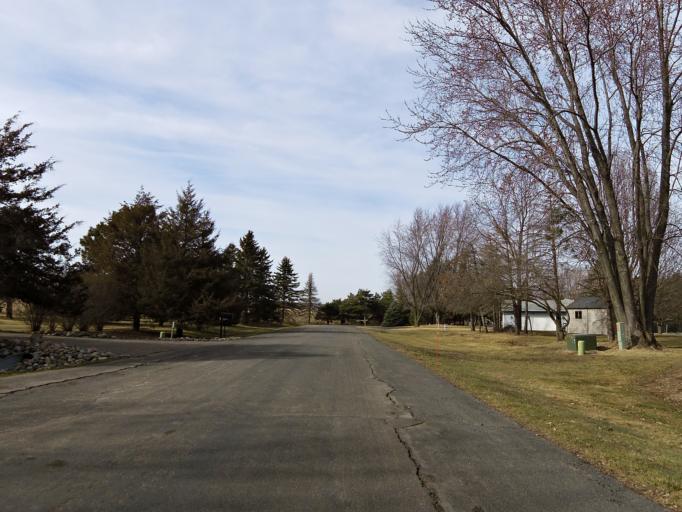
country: US
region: Minnesota
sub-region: Washington County
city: Lakeland
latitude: 44.9444
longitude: -92.7834
